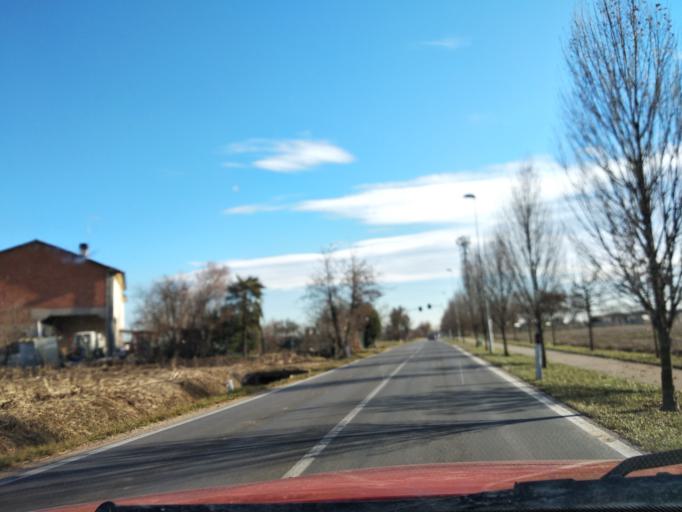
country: IT
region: Veneto
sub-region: Provincia di Vicenza
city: Motta
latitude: 45.5948
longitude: 11.5027
